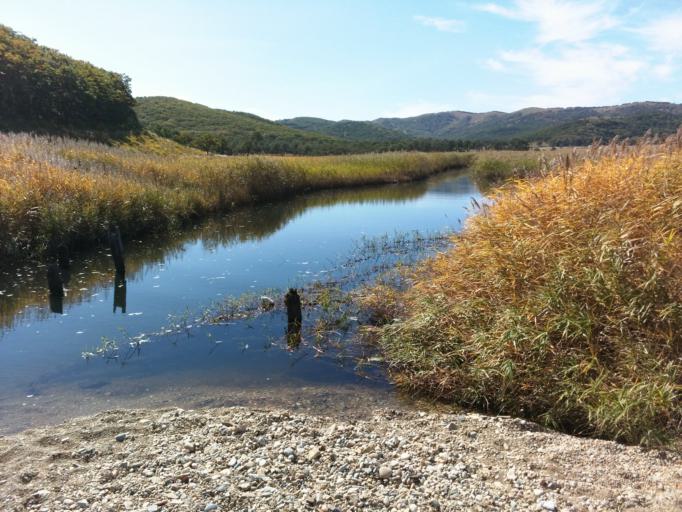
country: RU
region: Primorskiy
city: Zarubino
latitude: 42.6998
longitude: 131.2371
